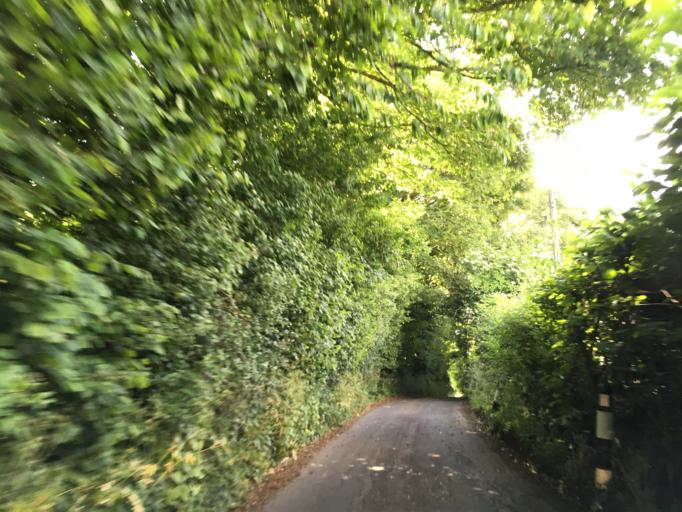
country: GB
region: England
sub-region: Gloucestershire
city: Brimscombe
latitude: 51.7218
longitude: -2.1903
